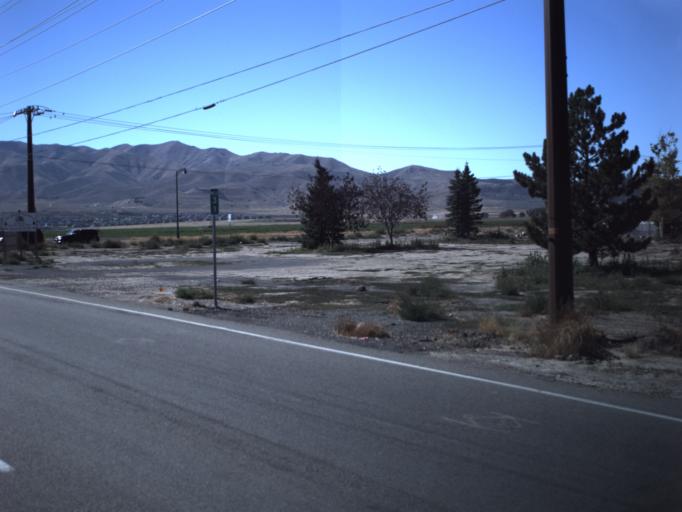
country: US
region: Utah
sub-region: Utah County
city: Saratoga Springs
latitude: 40.3628
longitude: -111.9163
